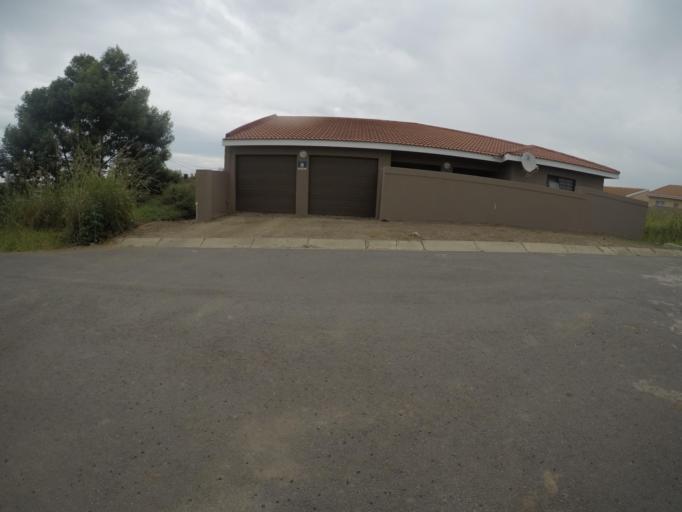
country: ZA
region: Eastern Cape
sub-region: Buffalo City Metropolitan Municipality
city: East London
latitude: -32.9935
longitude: 27.8442
